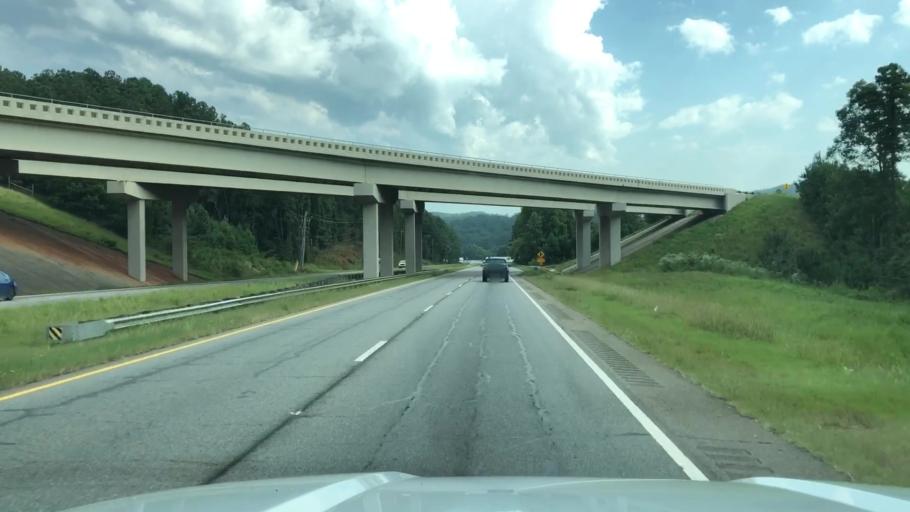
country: US
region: Georgia
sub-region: Bartow County
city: Emerson
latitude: 34.1379
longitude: -84.7501
